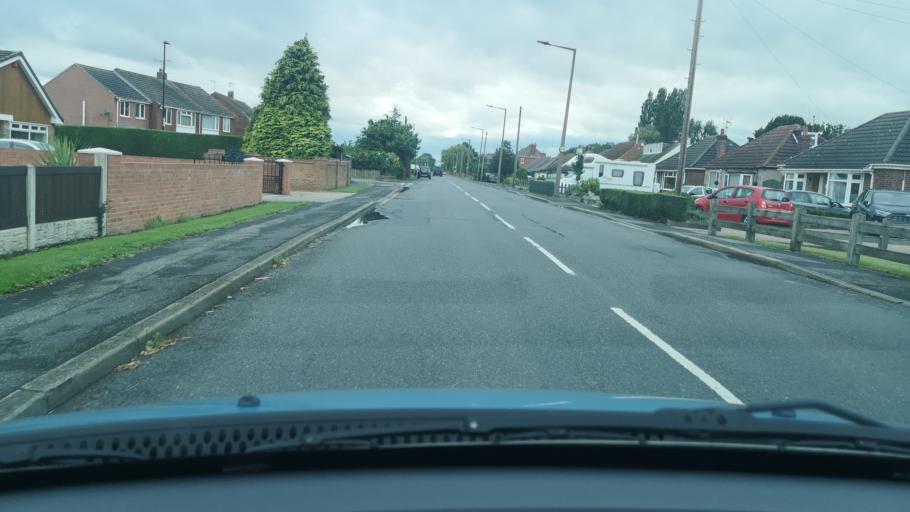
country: GB
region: England
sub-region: Doncaster
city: Hatfield
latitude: 53.6061
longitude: -0.9683
